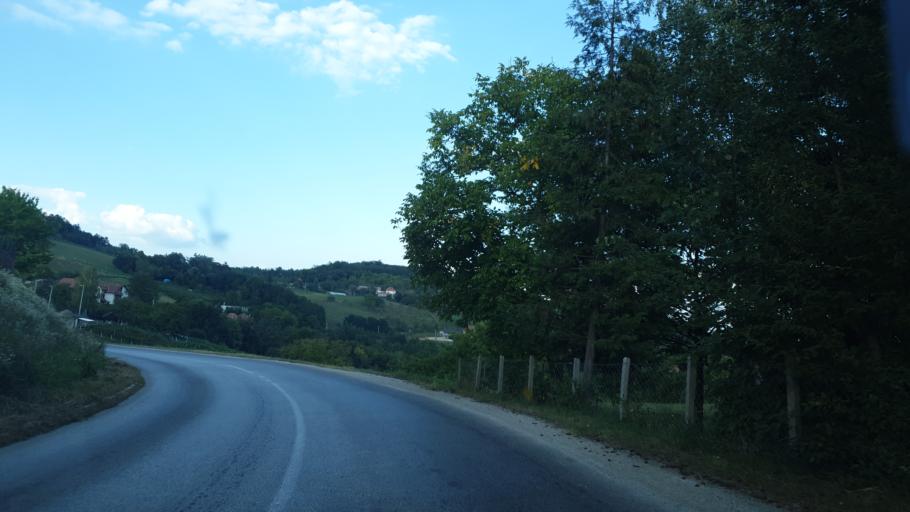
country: RS
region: Central Serbia
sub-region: Zlatiborski Okrug
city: Uzice
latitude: 43.8614
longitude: 19.8854
